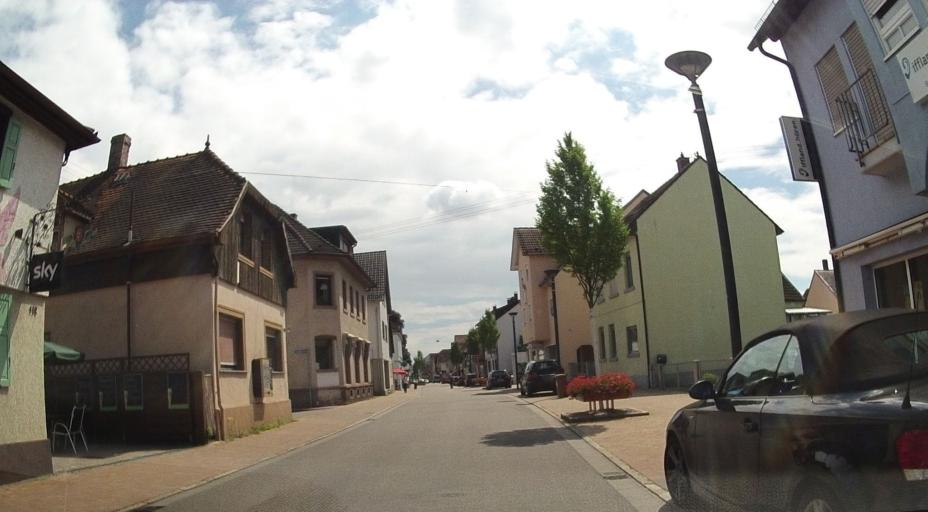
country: DE
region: Baden-Wuerttemberg
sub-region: Karlsruhe Region
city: Durmersheim
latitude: 48.9337
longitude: 8.2697
